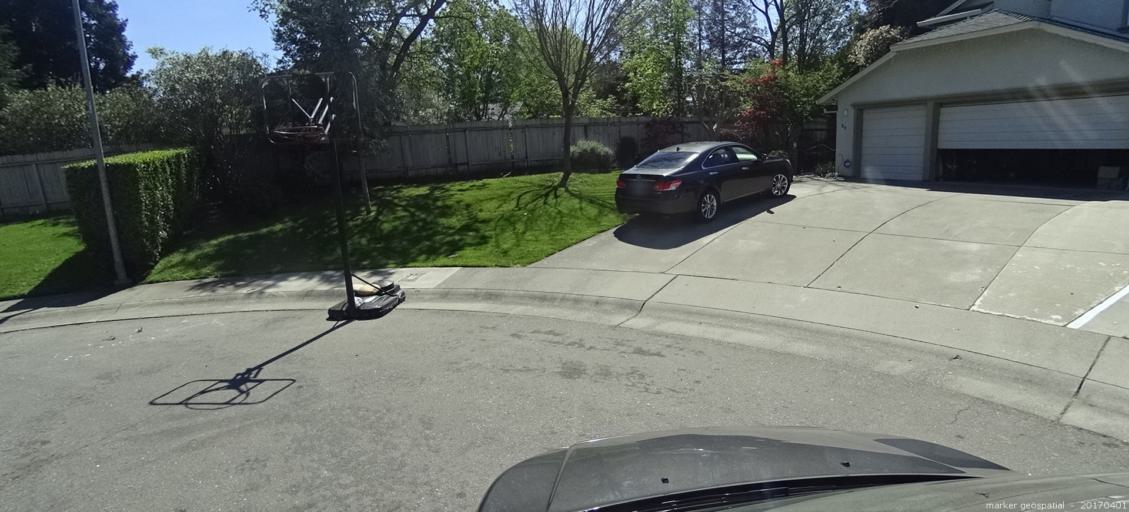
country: US
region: California
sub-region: Sacramento County
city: Laguna
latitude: 38.4468
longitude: -121.4312
